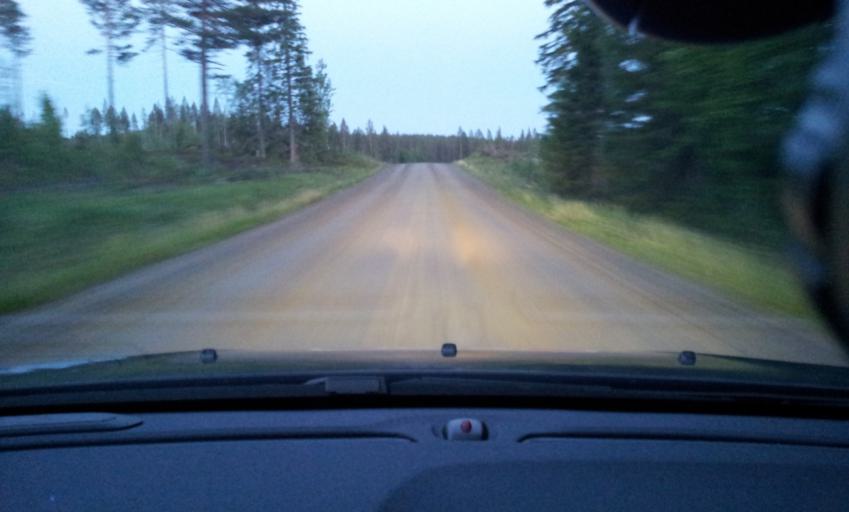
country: SE
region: Vaesternorrland
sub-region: Ange Kommun
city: Ange
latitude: 62.7387
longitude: 15.6421
